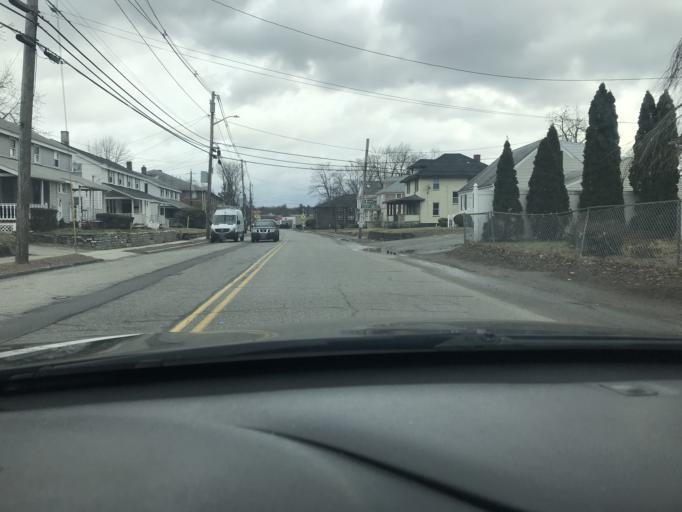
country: US
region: Massachusetts
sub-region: Middlesex County
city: Chelmsford
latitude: 42.6352
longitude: -71.3595
